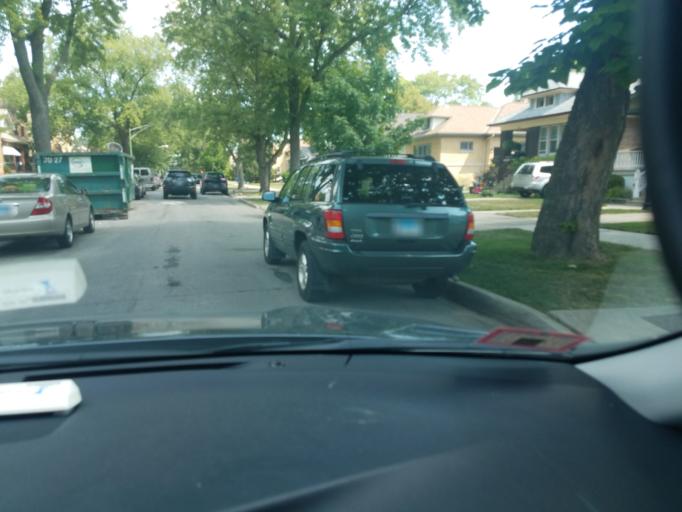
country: US
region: Illinois
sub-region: Cook County
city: Lincolnwood
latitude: 41.9636
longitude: -87.7386
